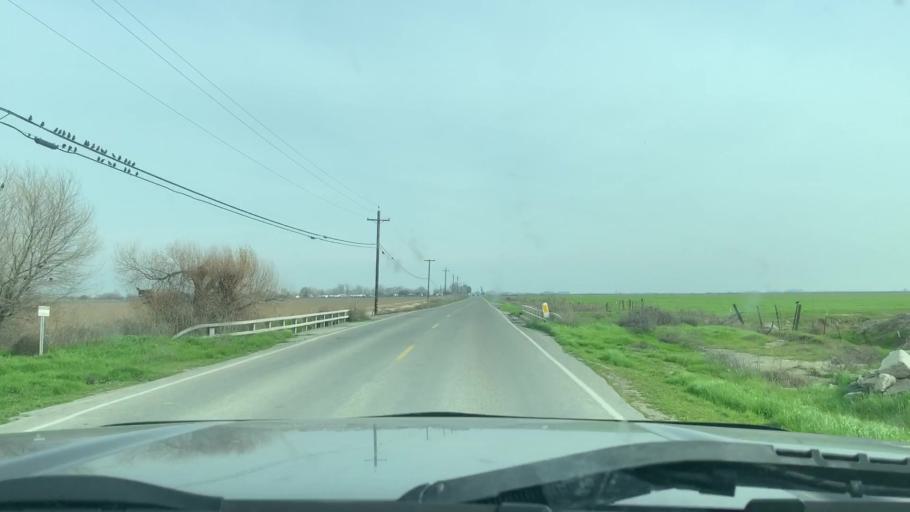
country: US
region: California
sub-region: Merced County
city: Los Banos
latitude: 37.0997
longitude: -120.8303
